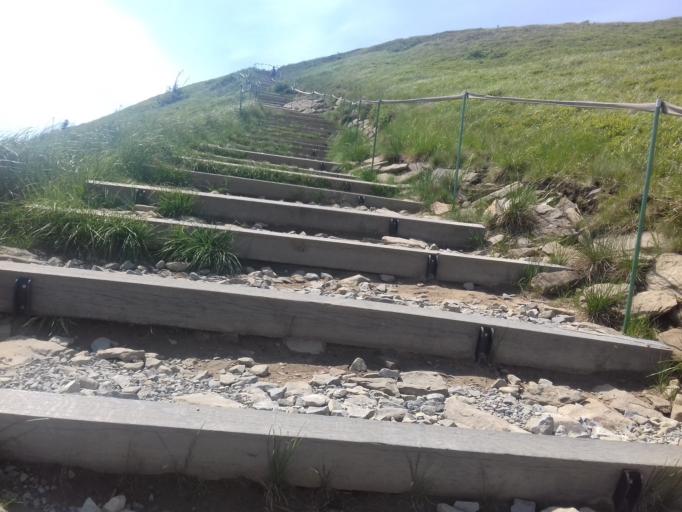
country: PL
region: Subcarpathian Voivodeship
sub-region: Powiat bieszczadzki
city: Lutowiska
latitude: 49.0762
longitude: 22.7265
